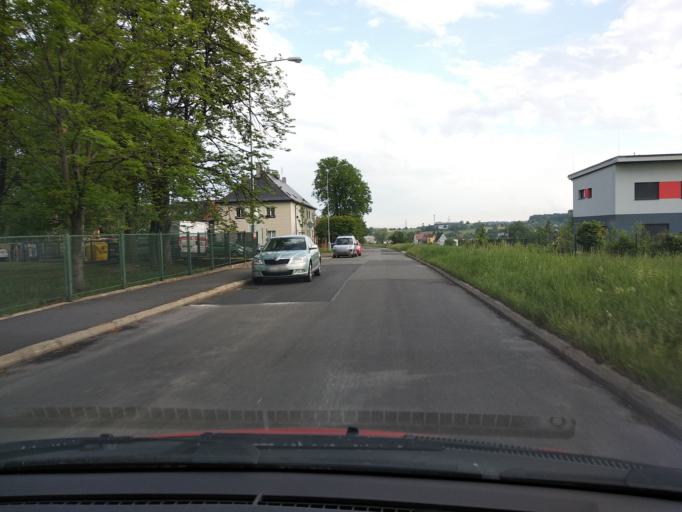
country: CZ
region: Moravskoslezsky
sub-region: Okres Frydek-Mistek
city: Frydek-Mistek
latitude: 49.6982
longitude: 18.3488
